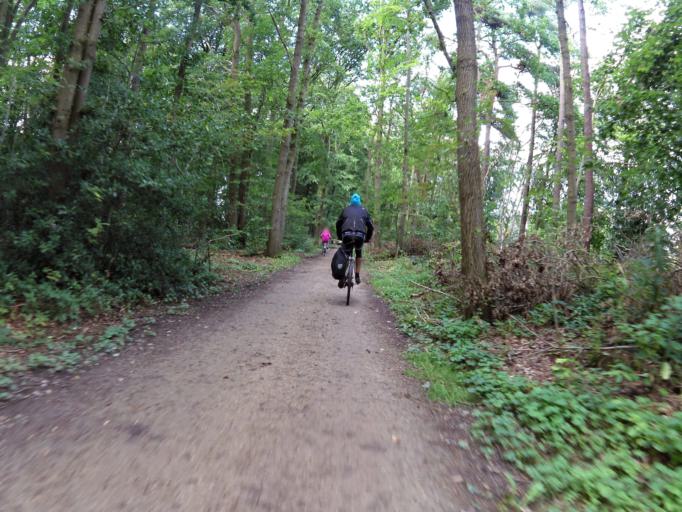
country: NL
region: Utrecht
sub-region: Gemeente Soest
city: Soest
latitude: 52.1672
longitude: 5.2636
